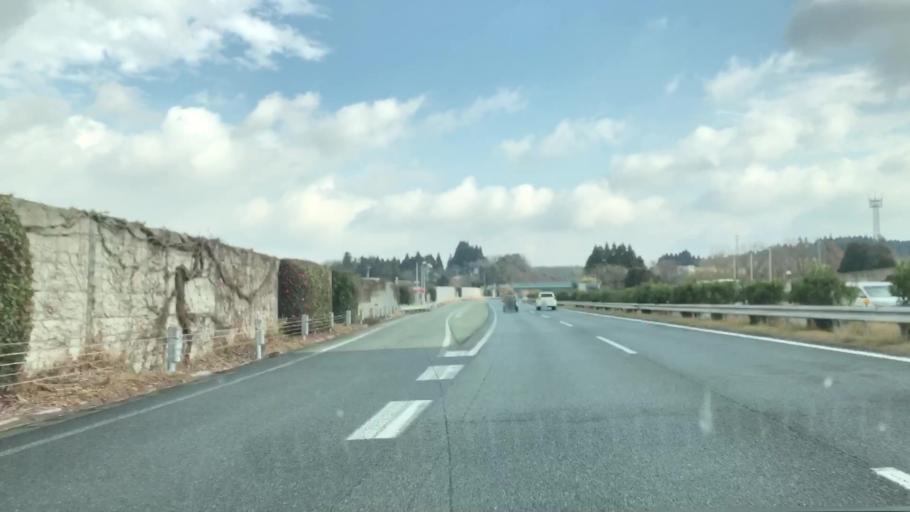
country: JP
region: Fukuoka
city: Omuta
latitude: 33.0442
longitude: 130.5631
